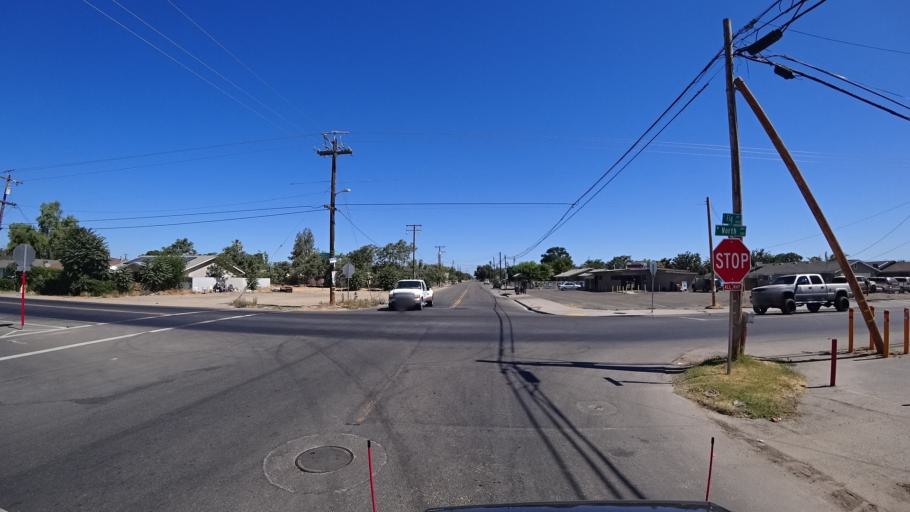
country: US
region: California
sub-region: Fresno County
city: Easton
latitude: 36.6922
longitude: -119.7998
